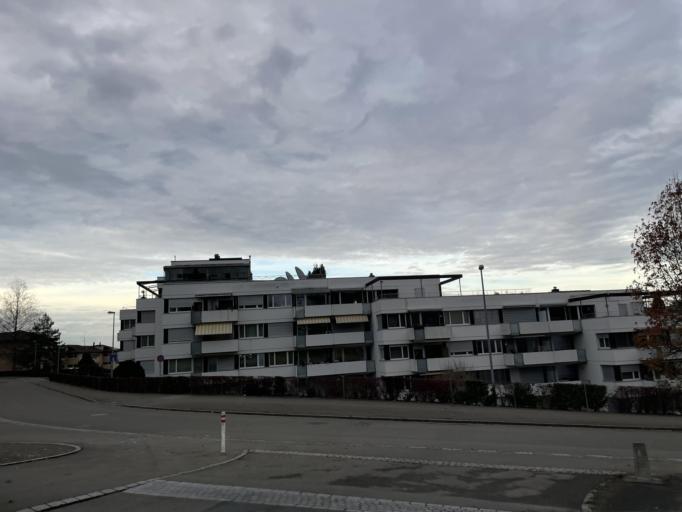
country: CH
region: Zurich
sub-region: Bezirk Buelach
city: Kloten / Spitz
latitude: 47.4452
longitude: 8.5872
